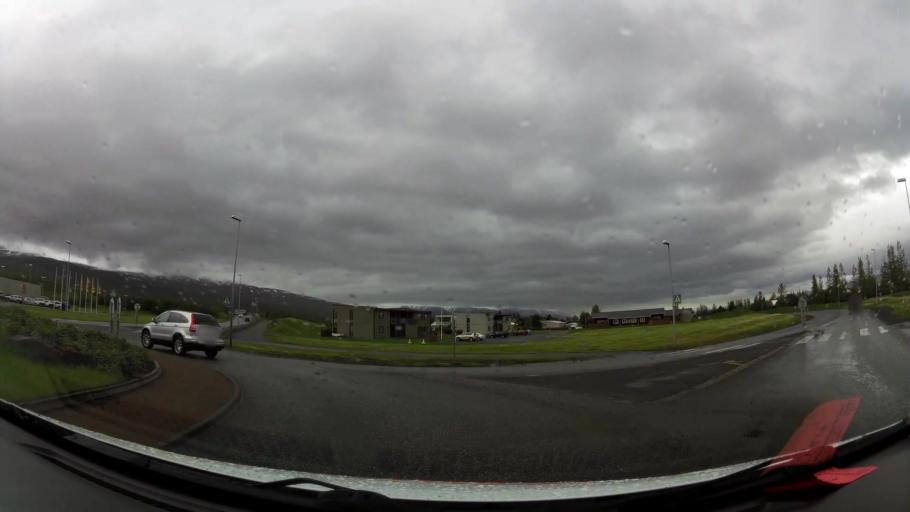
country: IS
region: Northeast
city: Akureyri
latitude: 65.6697
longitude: -18.1079
